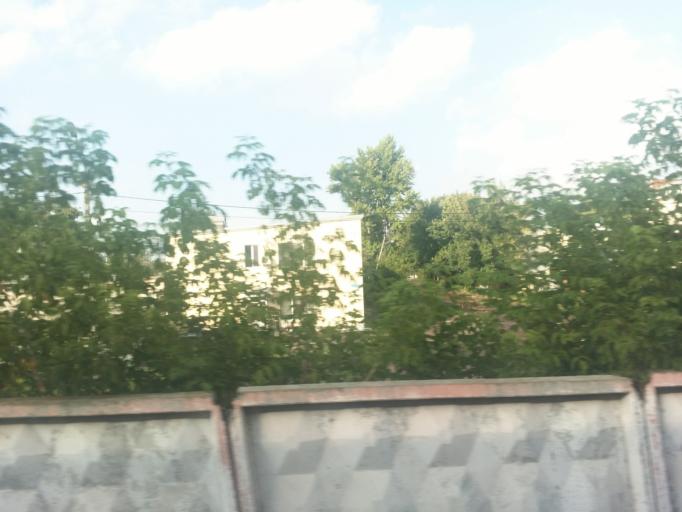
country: RU
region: Tatarstan
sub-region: Gorod Kazan'
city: Kazan
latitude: 55.8028
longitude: 49.0639
